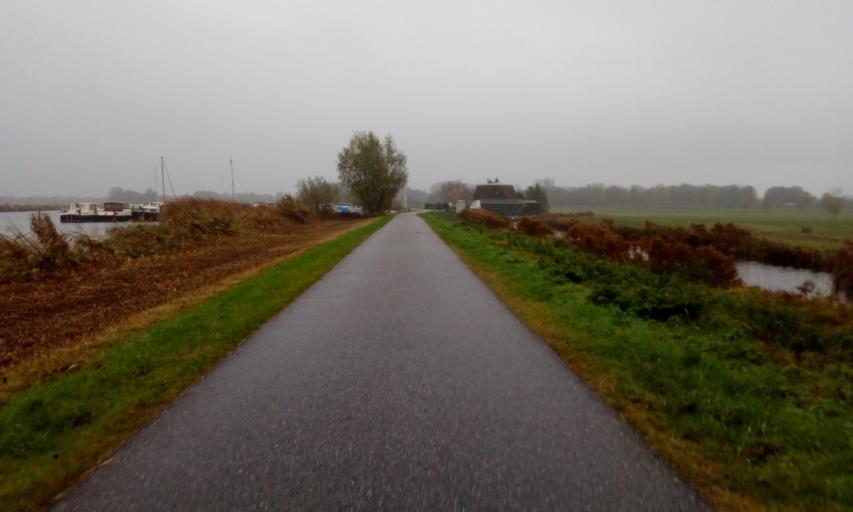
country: NL
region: South Holland
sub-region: Gemeente Lansingerland
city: Bleiswijk
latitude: 52.0198
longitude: 4.5561
